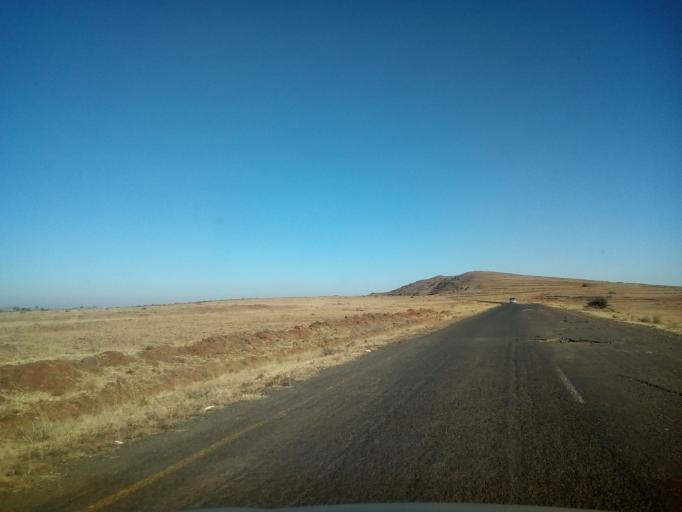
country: LS
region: Berea
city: Teyateyaneng
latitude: -29.2542
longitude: 27.7799
